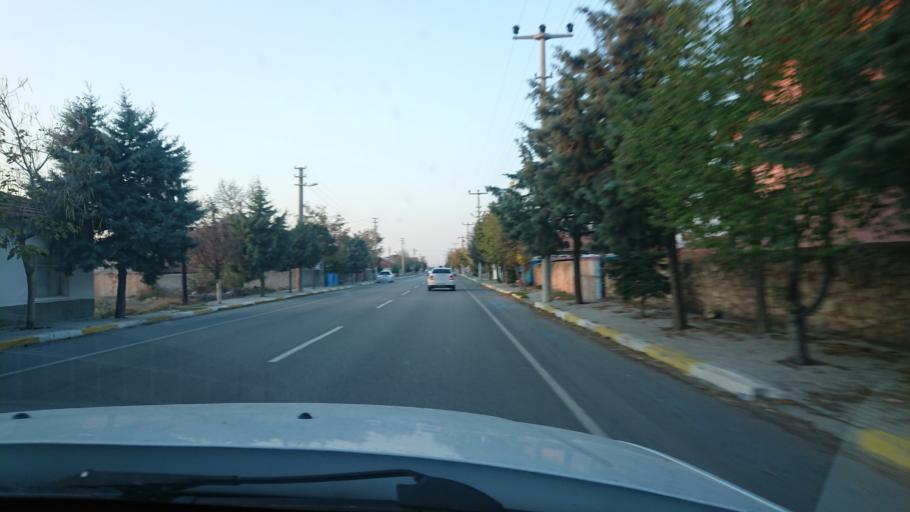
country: TR
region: Aksaray
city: Aksaray
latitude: 38.3061
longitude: 34.0681
